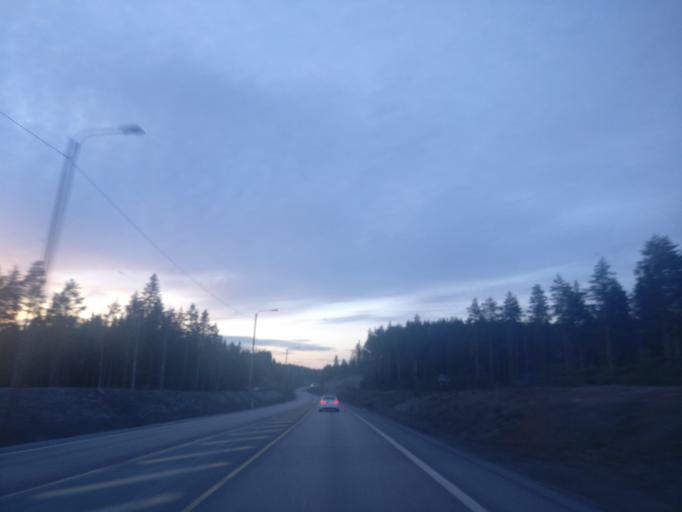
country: FI
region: Central Finland
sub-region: Jyvaeskylae
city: Saeynaetsalo
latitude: 62.1920
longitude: 25.9002
